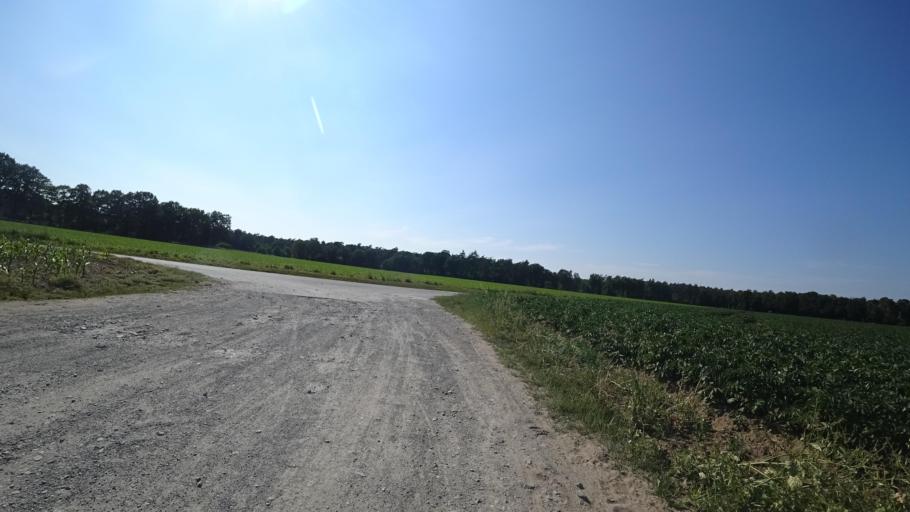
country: DE
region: North Rhine-Westphalia
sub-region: Regierungsbezirk Detmold
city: Rheda-Wiedenbruck
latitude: 51.8862
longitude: 8.3255
